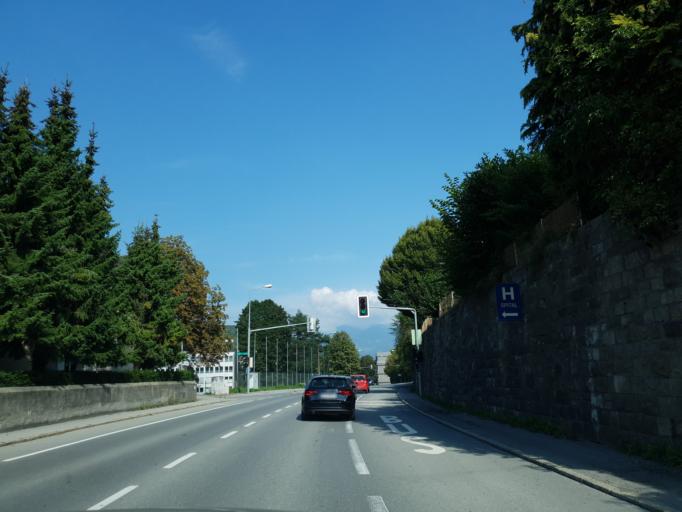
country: AT
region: Vorarlberg
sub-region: Politischer Bezirk Feldkirch
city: Feldkirch
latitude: 47.2323
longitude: 9.5875
